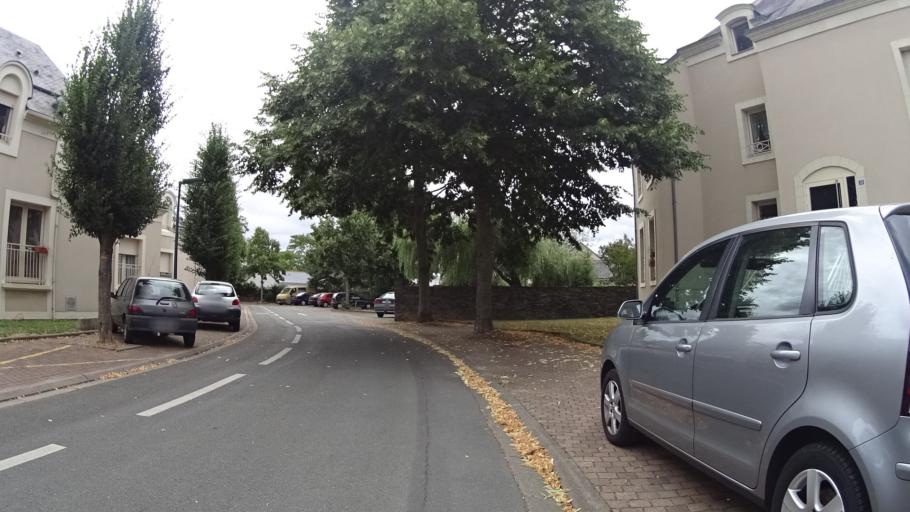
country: FR
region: Pays de la Loire
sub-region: Departement de Maine-et-Loire
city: Les Ponts-de-Ce
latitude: 47.4295
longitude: -0.5269
